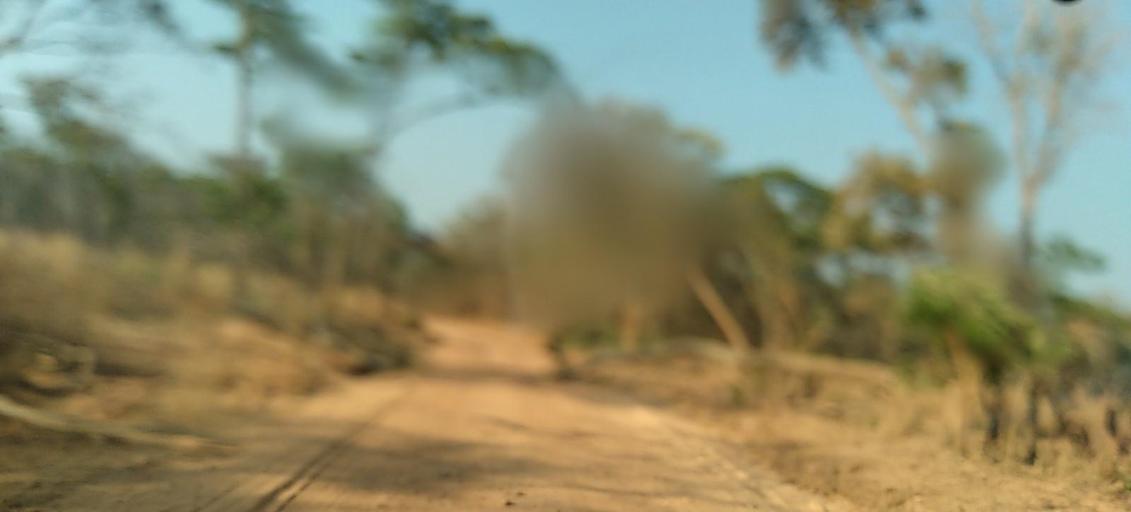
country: ZM
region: North-Western
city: Kasempa
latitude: -13.5742
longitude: 25.9922
